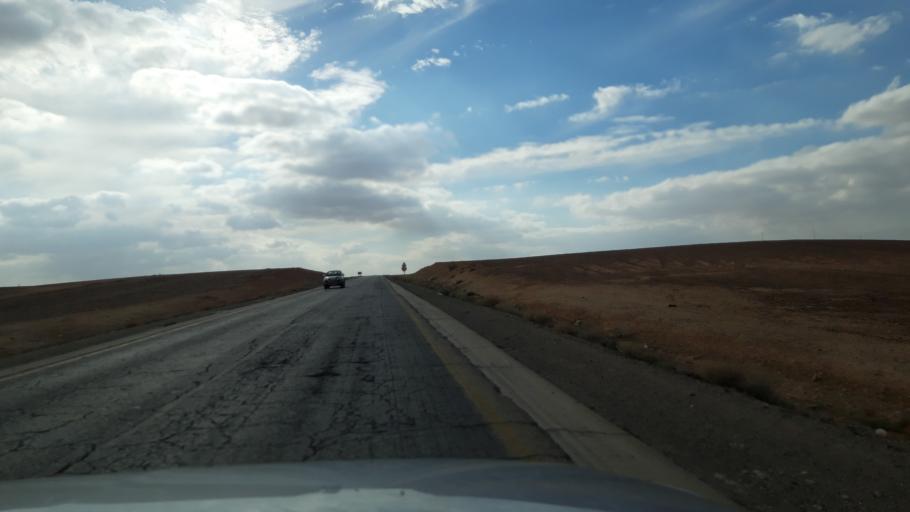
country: JO
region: Amman
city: Al Azraq ash Shamali
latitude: 31.7297
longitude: 36.4838
